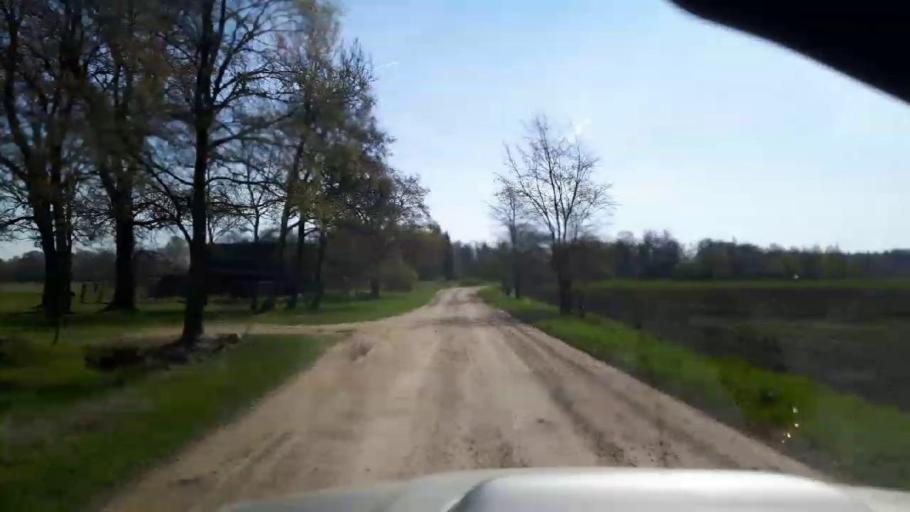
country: EE
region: Paernumaa
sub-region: Tootsi vald
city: Tootsi
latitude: 58.4851
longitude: 24.8999
